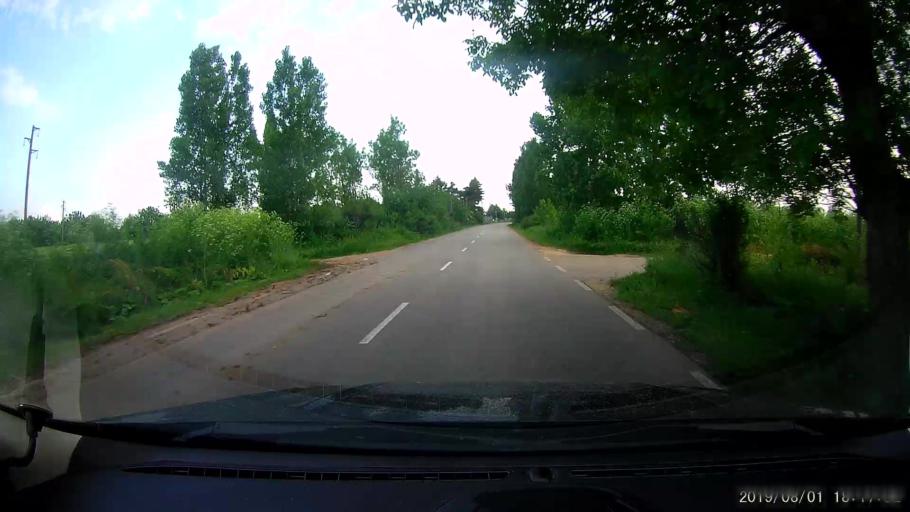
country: BG
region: Shumen
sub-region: Obshtina Kaolinovo
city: Kaolinovo
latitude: 43.7049
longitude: 27.0811
